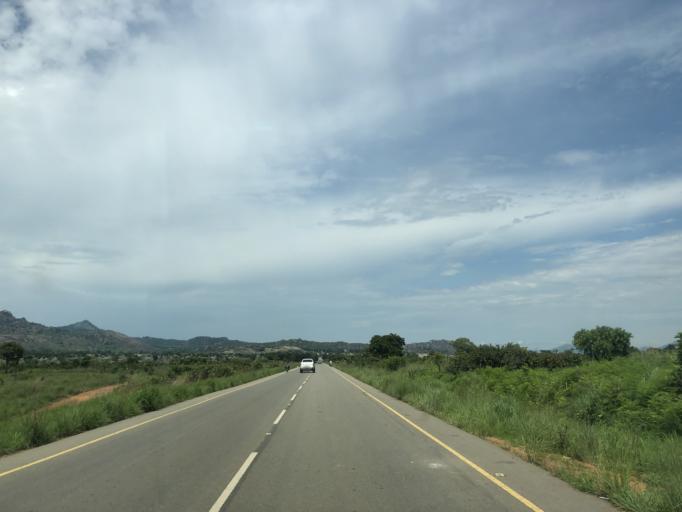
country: AO
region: Cuanza Sul
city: Quibala
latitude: -10.7346
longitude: 15.0049
